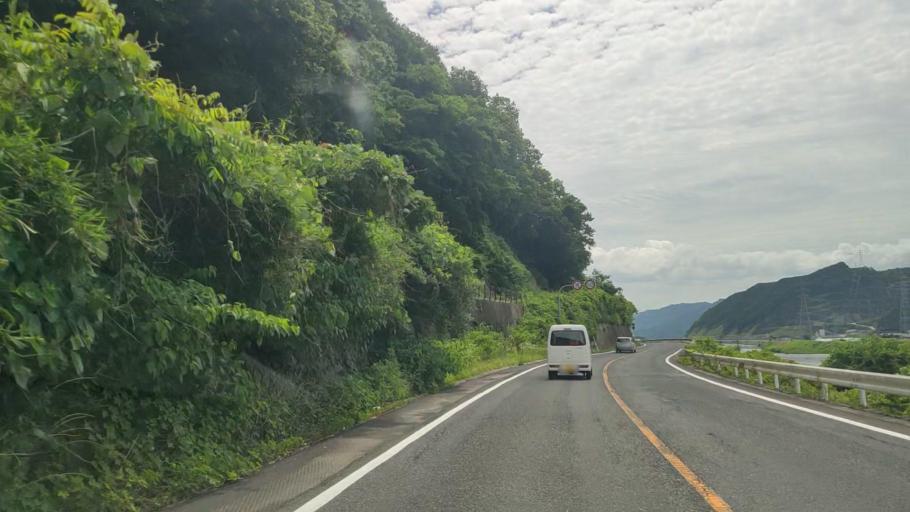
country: JP
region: Okayama
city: Niimi
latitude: 35.0836
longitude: 133.7202
